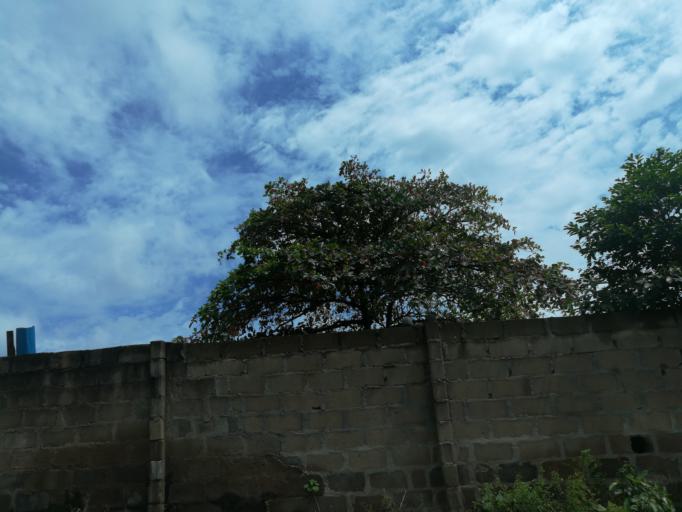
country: NG
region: Lagos
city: Agege
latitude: 6.6061
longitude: 3.3303
